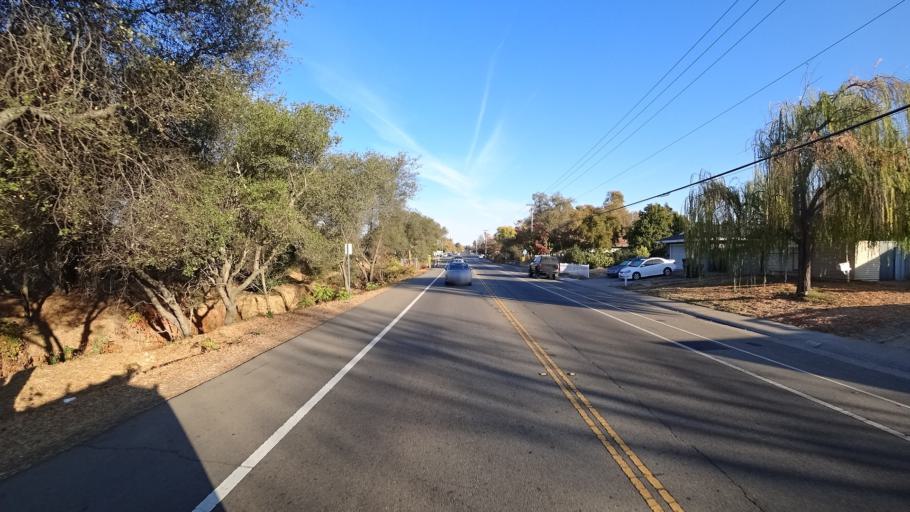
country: US
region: California
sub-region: Sacramento County
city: Antelope
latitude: 38.6978
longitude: -121.3087
